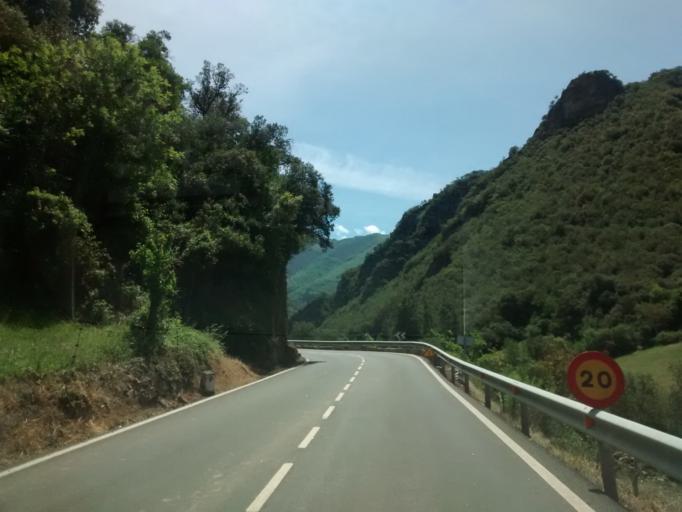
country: ES
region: Cantabria
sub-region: Provincia de Cantabria
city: Potes
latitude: 43.1309
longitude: -4.6309
